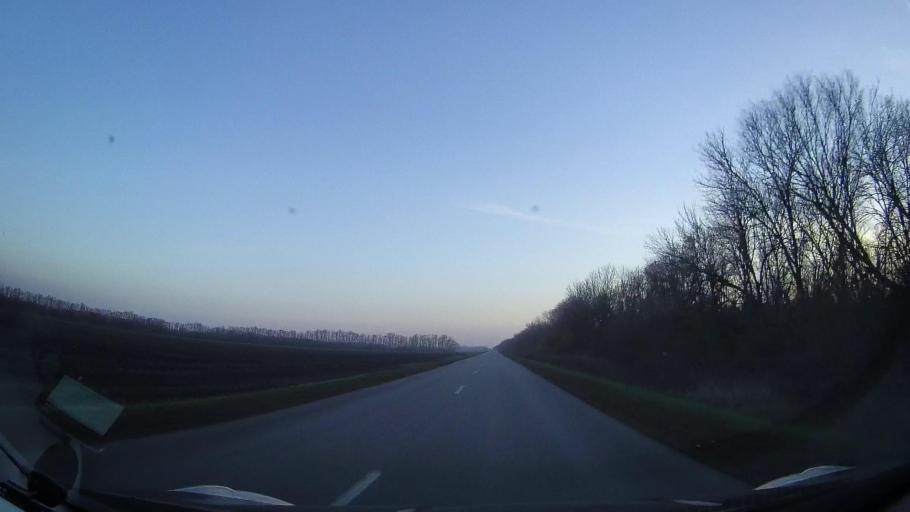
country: RU
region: Rostov
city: Zernograd
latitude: 47.0140
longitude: 40.3916
